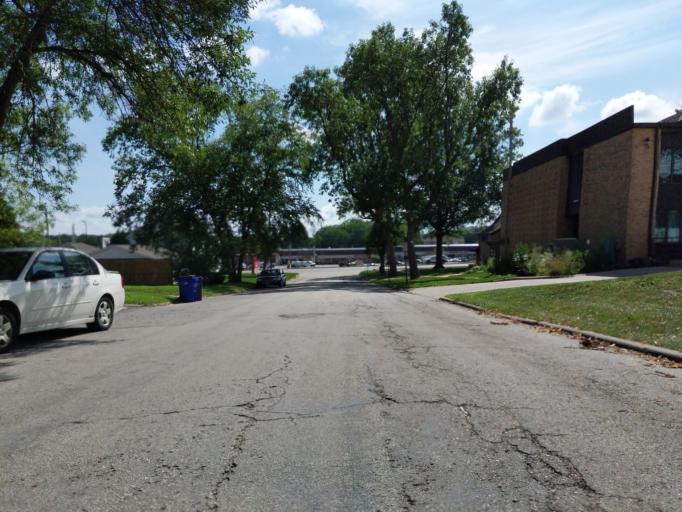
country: US
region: Iowa
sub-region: Linn County
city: Cedar Rapids
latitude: 42.0159
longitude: -91.6363
